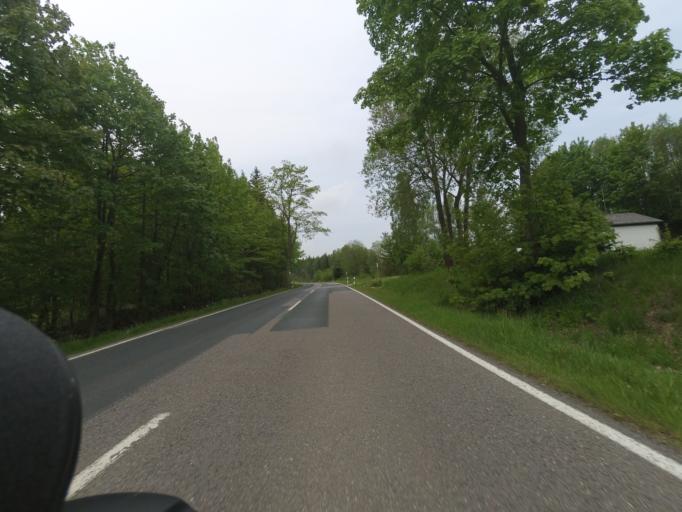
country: DE
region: Saxony
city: Marienberg
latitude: 50.6514
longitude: 13.1413
